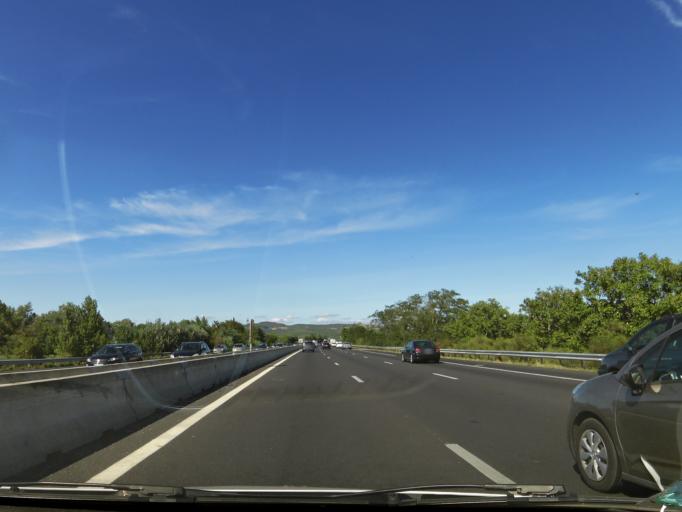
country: FR
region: Provence-Alpes-Cote d'Azur
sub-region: Departement du Vaucluse
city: Bollene
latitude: 44.2773
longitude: 4.7308
